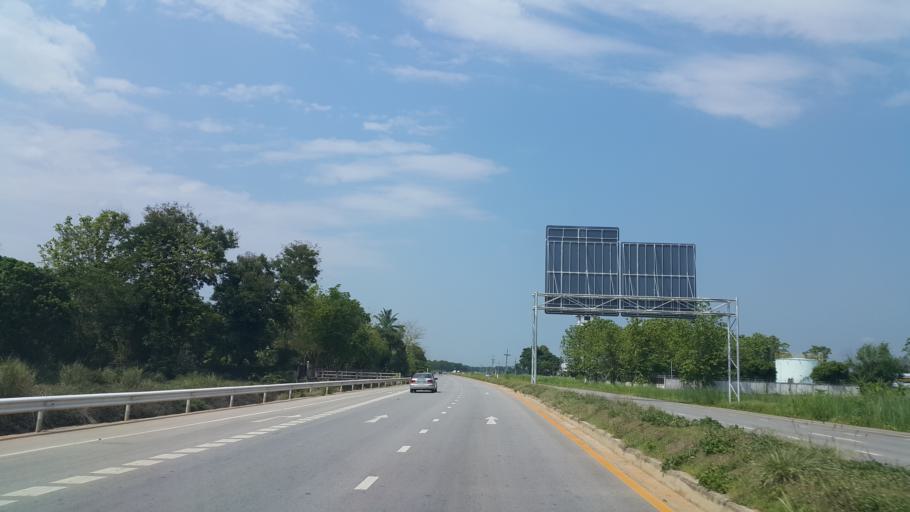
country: TH
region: Chiang Rai
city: Chiang Rai
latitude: 19.9698
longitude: 99.8864
